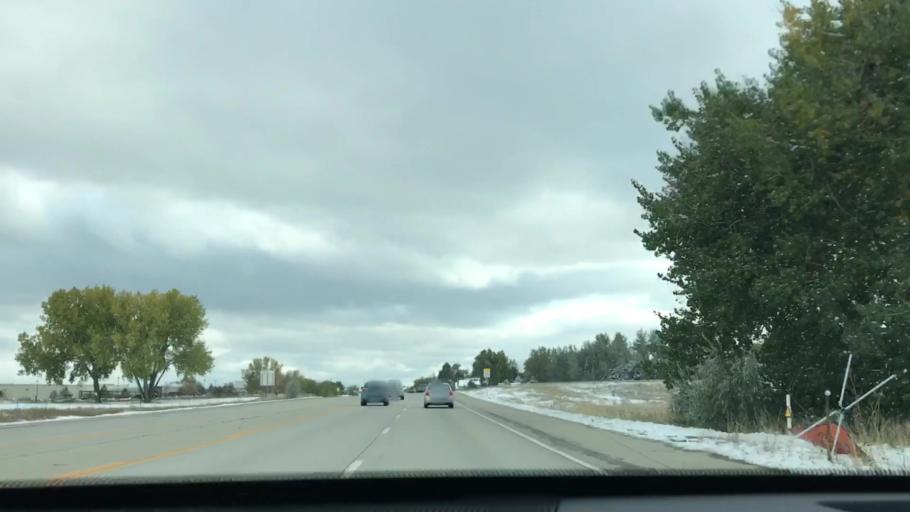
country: US
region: Colorado
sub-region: Boulder County
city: Lafayette
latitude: 40.0212
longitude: -105.1029
